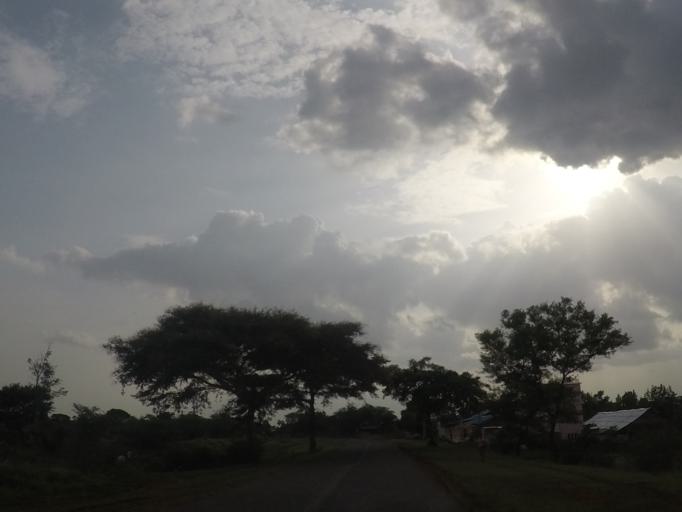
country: MM
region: Mandalay
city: Meiktila
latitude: 20.5379
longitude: 95.6673
